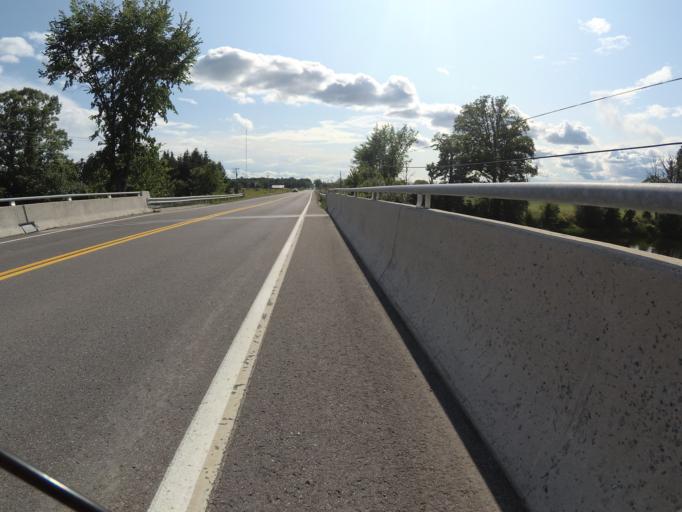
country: CA
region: Ontario
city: Arnprior
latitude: 45.4688
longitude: -76.1835
